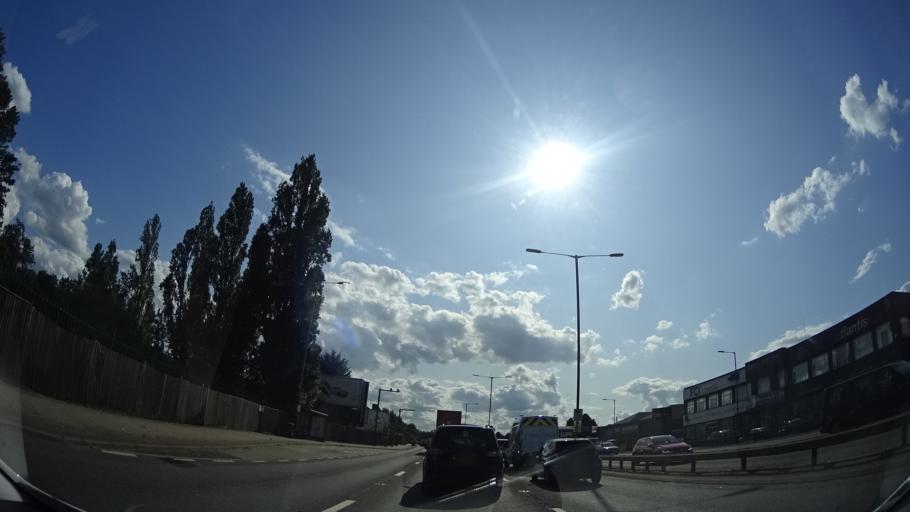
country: GB
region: England
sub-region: Greater London
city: Wembley
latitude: 51.5358
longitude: -0.2867
